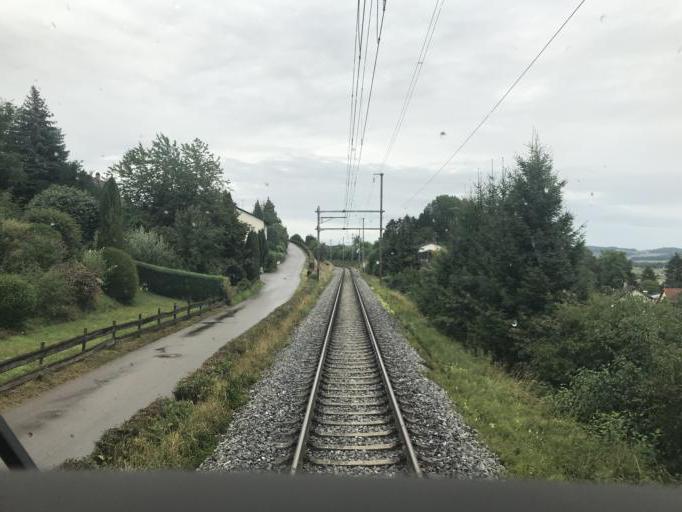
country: DE
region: Baden-Wuerttemberg
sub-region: Freiburg Region
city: Lottstetten
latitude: 47.6286
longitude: 8.5717
